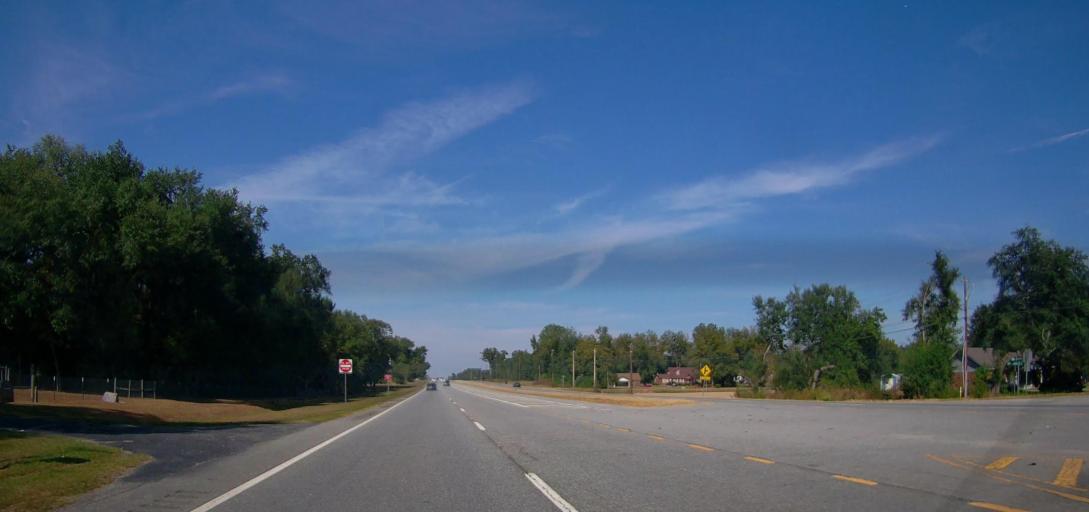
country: US
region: Georgia
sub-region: Dougherty County
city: Putney
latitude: 31.5029
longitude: -84.1156
